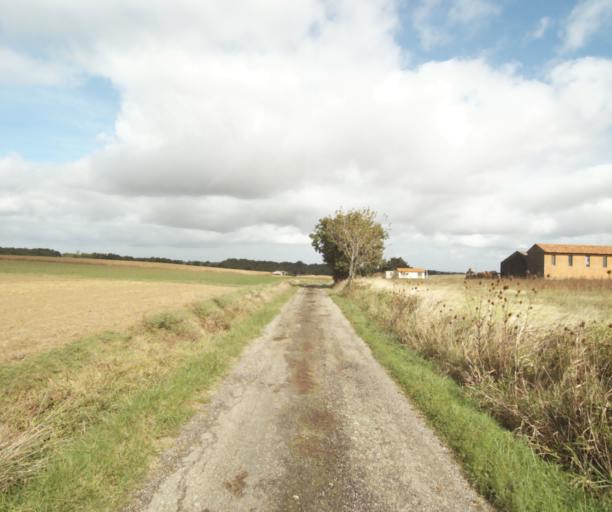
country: FR
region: Midi-Pyrenees
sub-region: Departement du Tarn-et-Garonne
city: Beaumont-de-Lomagne
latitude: 43.8661
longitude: 1.0789
